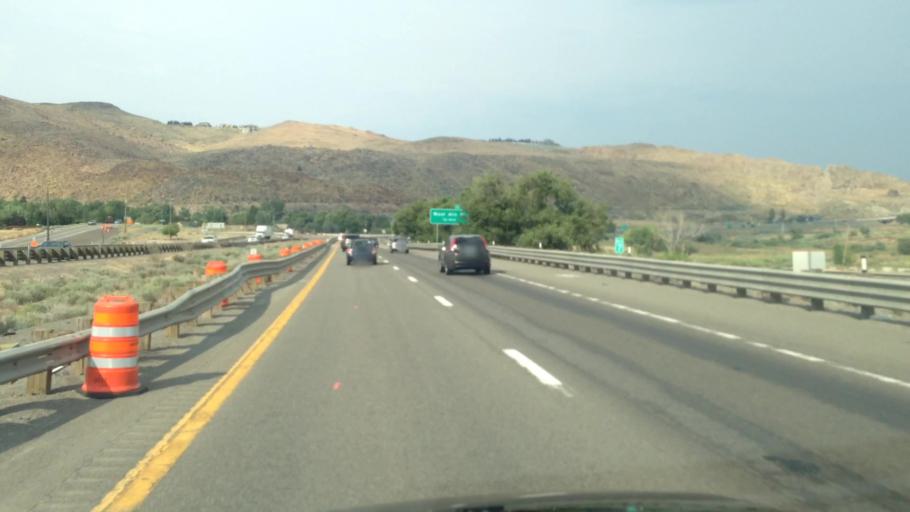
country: US
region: Nevada
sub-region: Washoe County
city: Mogul
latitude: 39.5136
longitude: -119.9276
